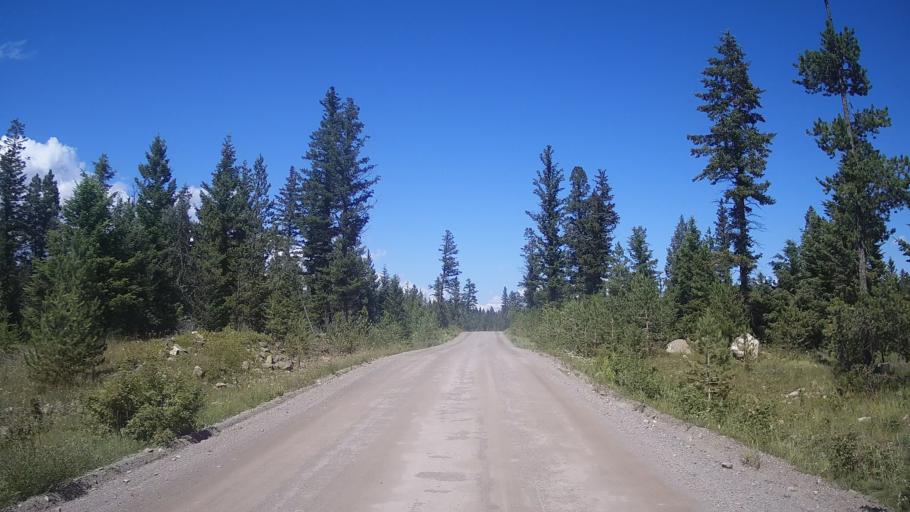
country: CA
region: British Columbia
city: Cache Creek
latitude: 51.1669
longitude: -121.5632
